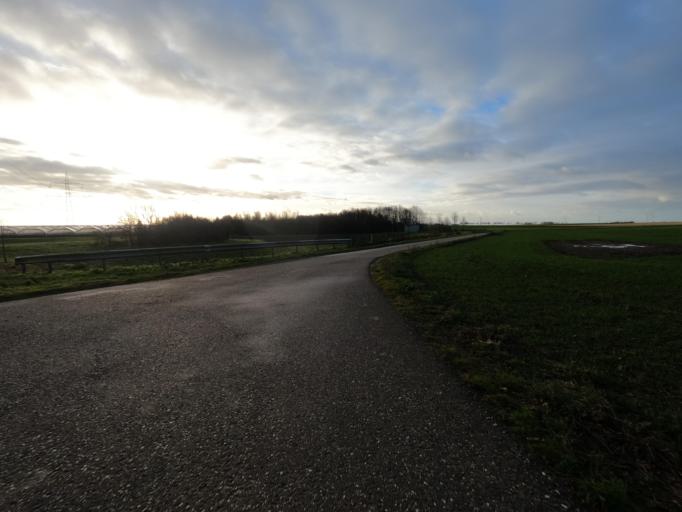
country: DE
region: North Rhine-Westphalia
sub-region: Regierungsbezirk Koln
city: Heinsberg
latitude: 51.0682
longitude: 6.0681
